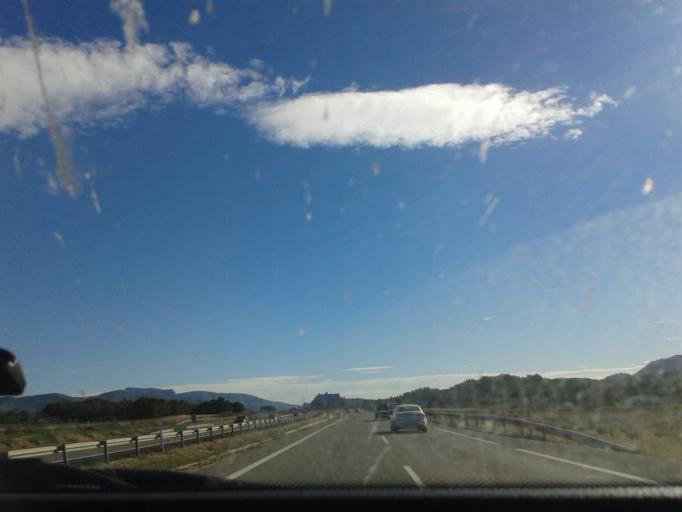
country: ES
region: Valencia
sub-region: Provincia de Alicante
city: Sax
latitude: 38.5670
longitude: -0.8353
